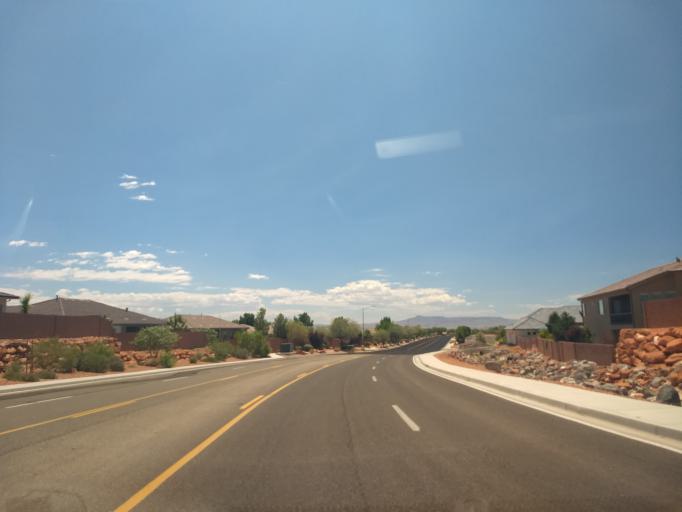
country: US
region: Utah
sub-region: Washington County
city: Washington
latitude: 37.1572
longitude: -113.5260
